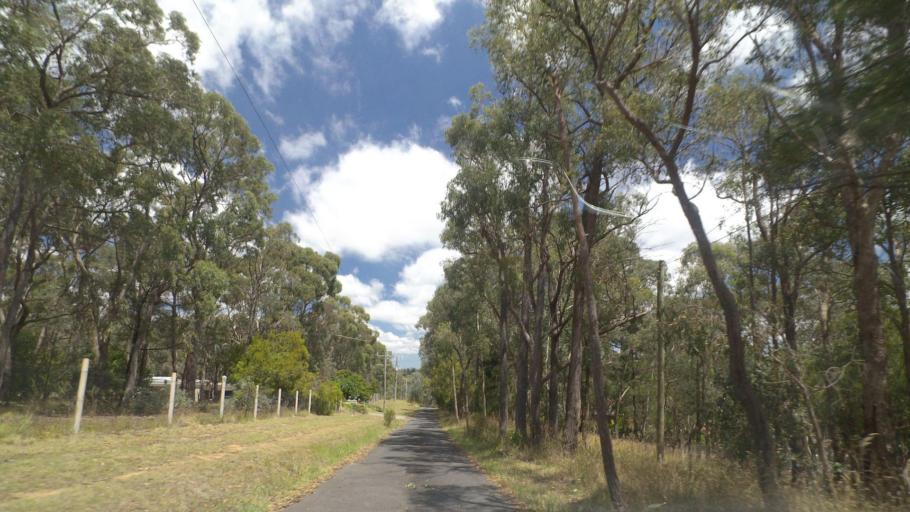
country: AU
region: Victoria
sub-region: Manningham
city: Warrandyte
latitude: -37.7451
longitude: 145.2636
